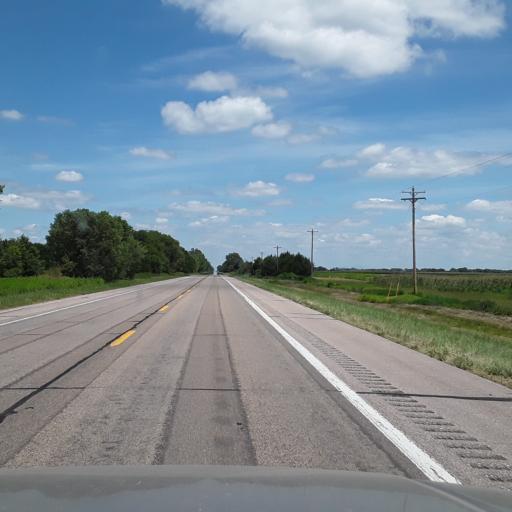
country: US
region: Nebraska
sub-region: Platte County
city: Columbus
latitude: 41.3733
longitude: -97.5286
